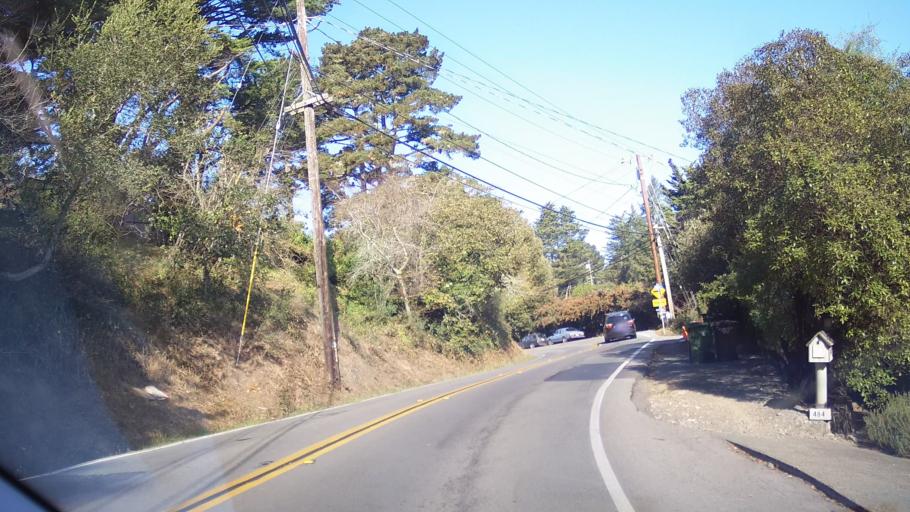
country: US
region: California
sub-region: Marin County
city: Mill Valley
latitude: 37.9005
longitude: -122.5667
